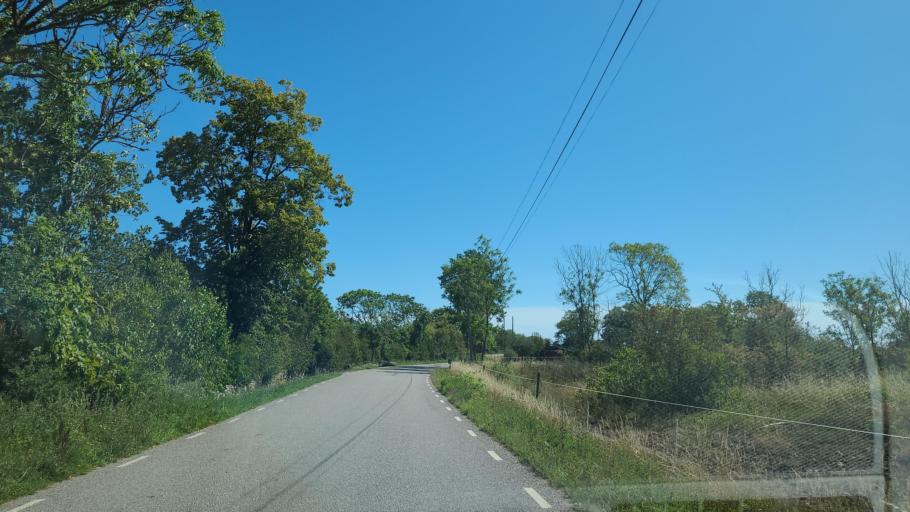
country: SE
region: Kalmar
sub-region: Borgholms Kommun
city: Borgholm
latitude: 56.7673
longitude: 16.6073
